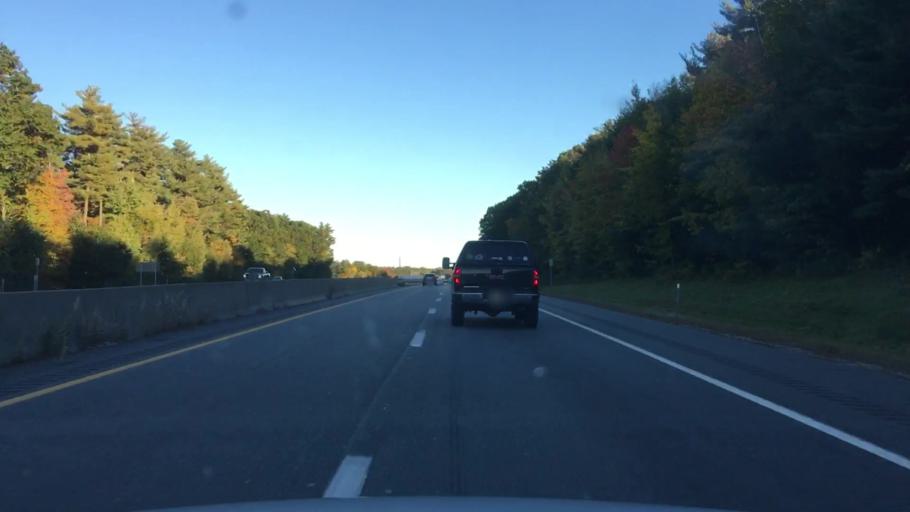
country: US
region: New Hampshire
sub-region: Rockingham County
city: Hampton
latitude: 42.9633
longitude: -70.8714
